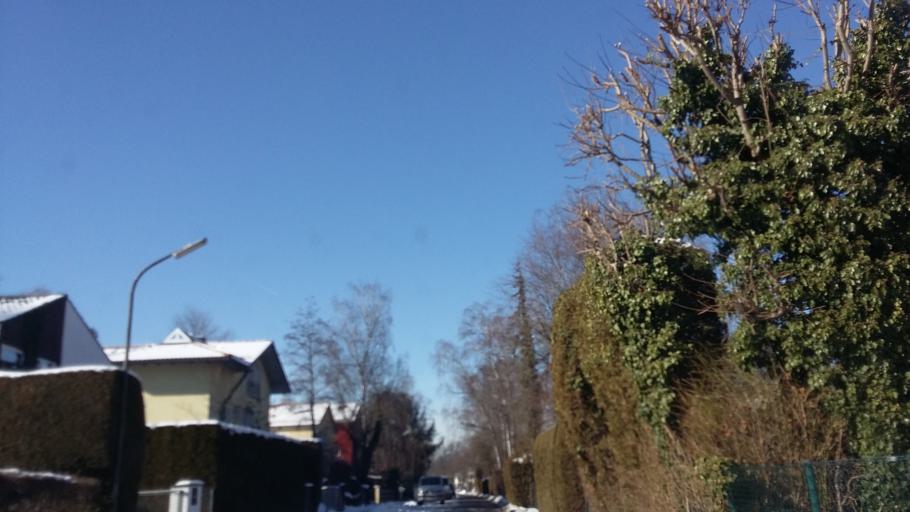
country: DE
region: Bavaria
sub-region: Upper Bavaria
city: Grafelfing
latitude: 48.1070
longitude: 11.4313
